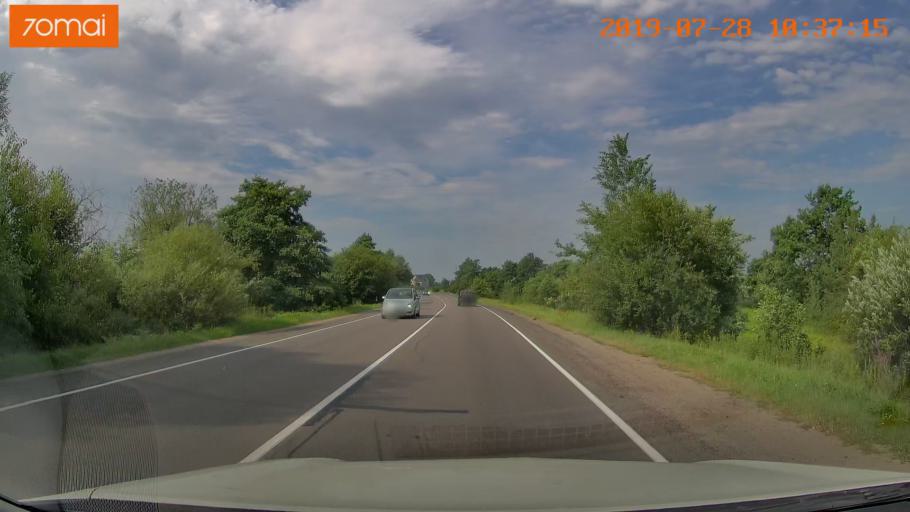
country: RU
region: Kaliningrad
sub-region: Gorod Kaliningrad
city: Kaliningrad
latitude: 54.7325
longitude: 20.4113
